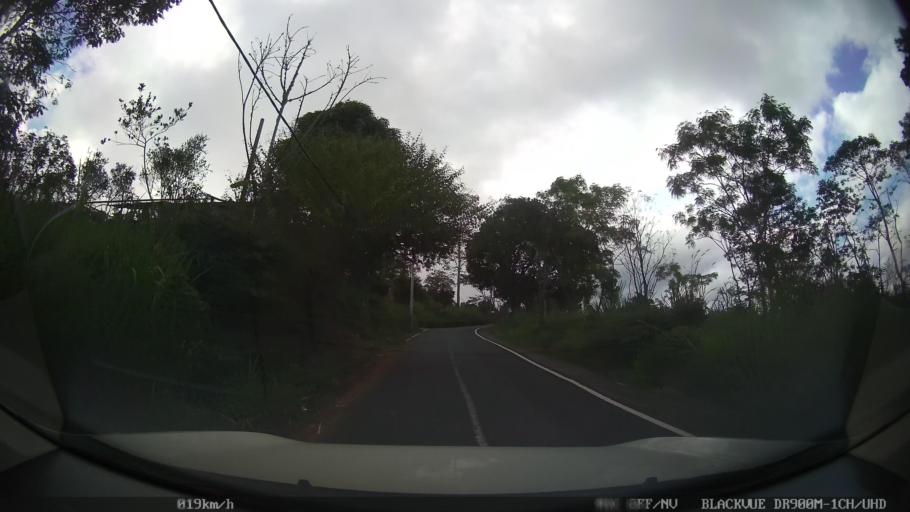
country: ID
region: Bali
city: Banjar Kedisan
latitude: -8.2587
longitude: 115.3447
